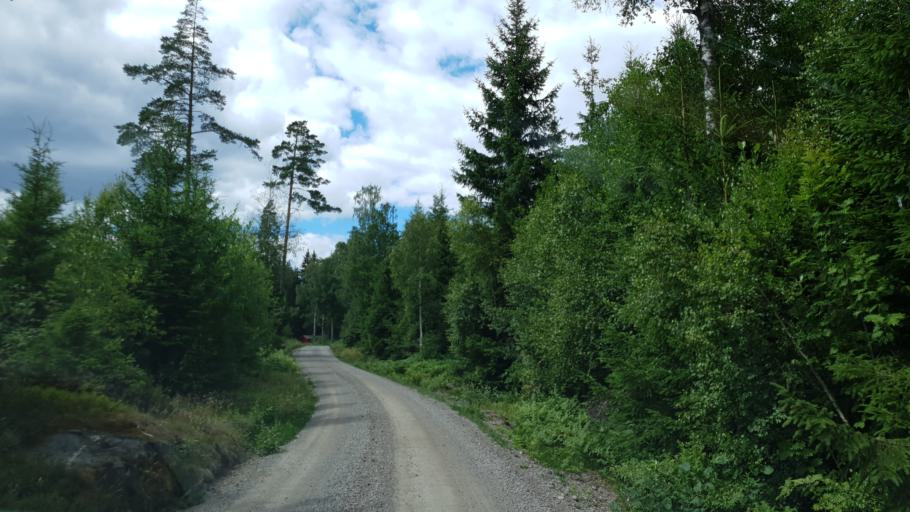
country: SE
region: Kalmar
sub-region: Hultsfreds Kommun
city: Virserum
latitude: 57.0936
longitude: 15.6357
